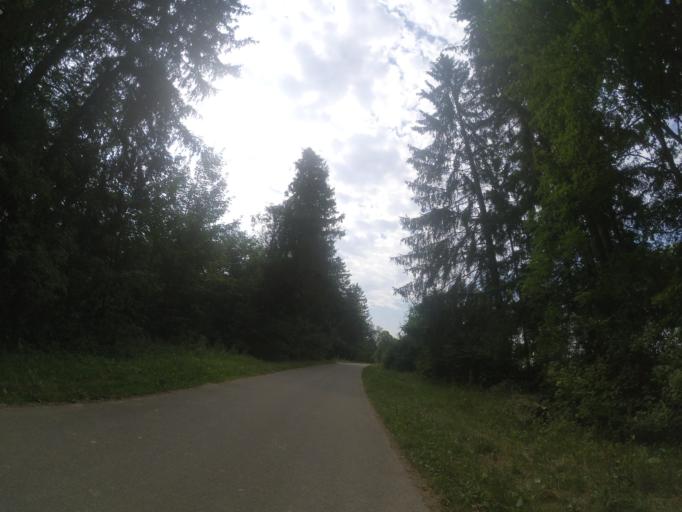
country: DE
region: Baden-Wuerttemberg
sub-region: Tuebingen Region
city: Dornstadt
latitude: 48.4941
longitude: 9.9011
